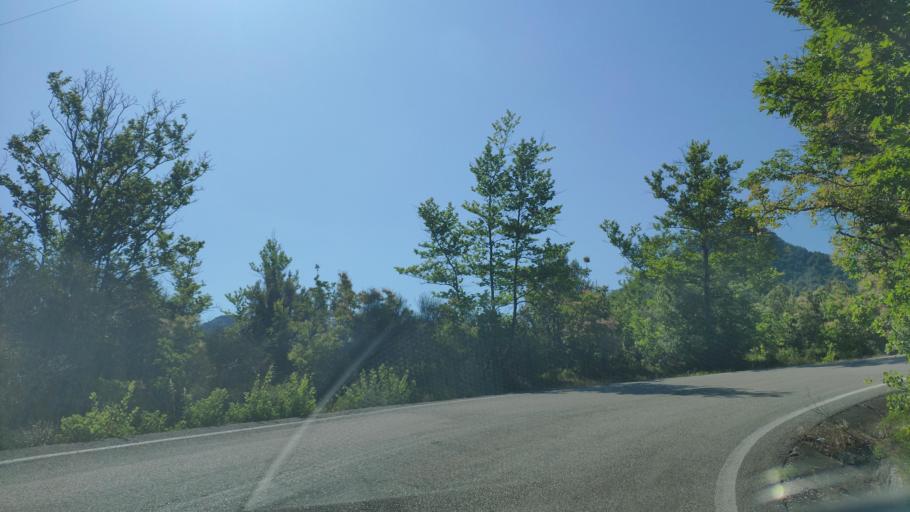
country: GR
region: West Greece
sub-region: Nomos Aitolias kai Akarnanias
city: Sardinia
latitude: 38.9255
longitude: 21.3908
